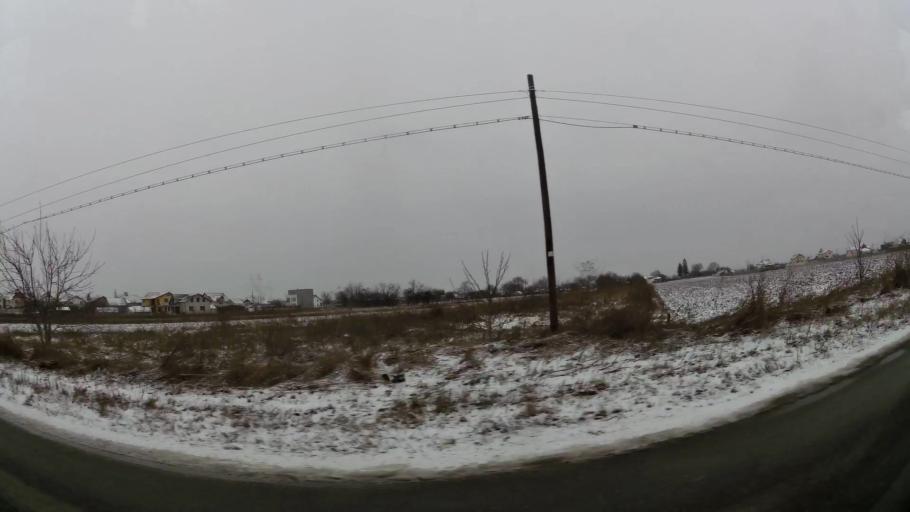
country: RO
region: Dambovita
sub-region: Comuna Ulmi
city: Ulmi
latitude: 44.8907
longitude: 25.5185
